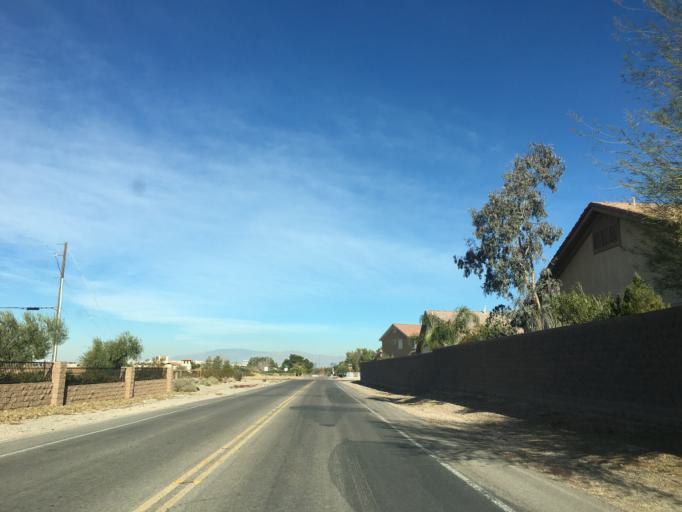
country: US
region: Nevada
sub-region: Clark County
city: Enterprise
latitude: 36.0052
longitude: -115.1658
